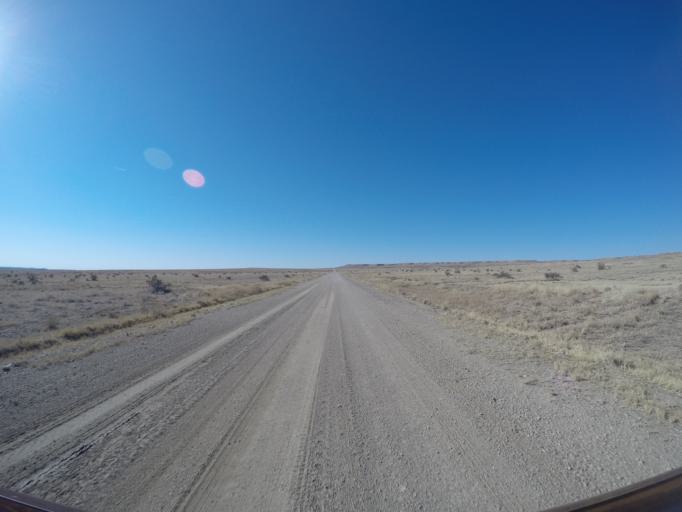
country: US
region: Colorado
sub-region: Otero County
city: La Junta
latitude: 37.7751
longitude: -103.5537
